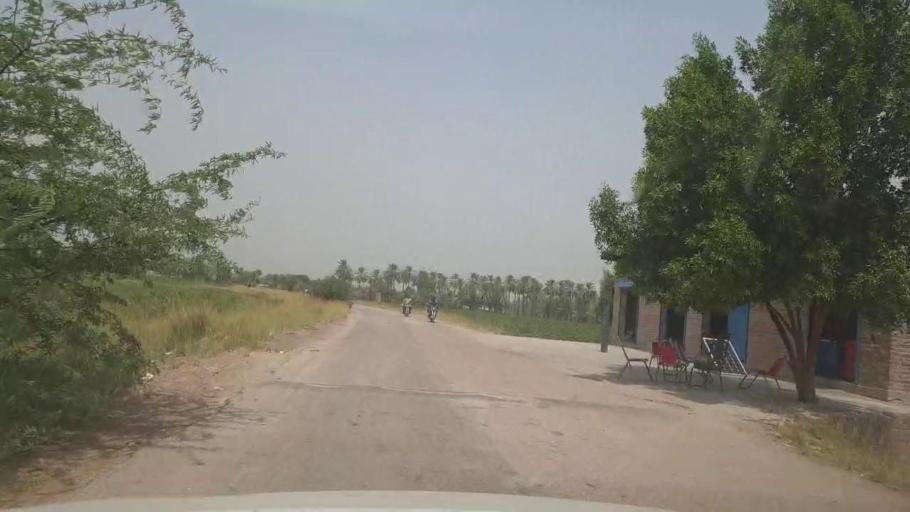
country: PK
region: Sindh
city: Kot Diji
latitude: 27.3626
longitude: 68.6731
